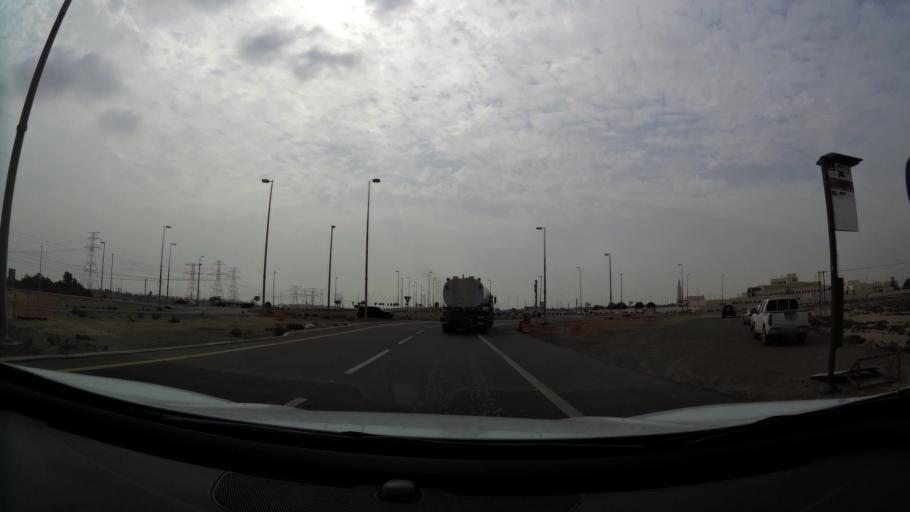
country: AE
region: Abu Dhabi
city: Abu Dhabi
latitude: 24.6607
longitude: 54.7439
